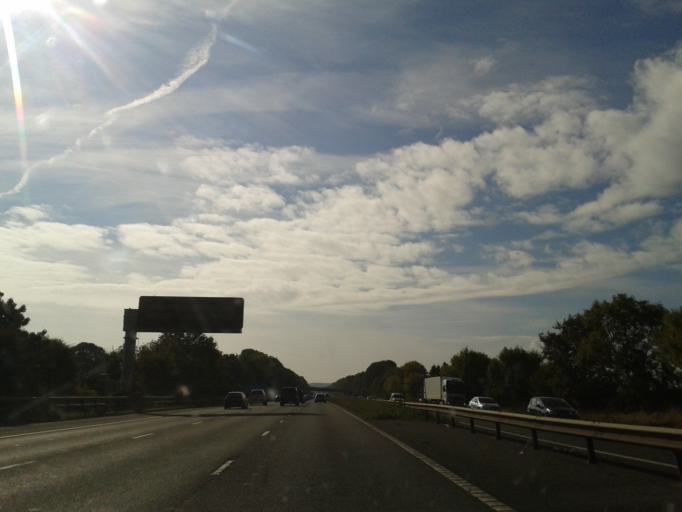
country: GB
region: England
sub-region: Staffordshire
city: Audley
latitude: 53.0592
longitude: -2.3315
